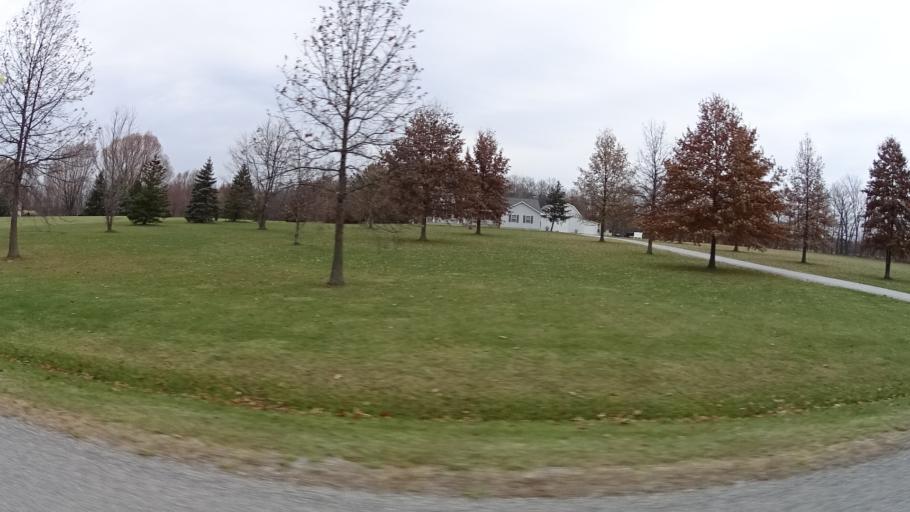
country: US
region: Ohio
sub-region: Lorain County
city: Lagrange
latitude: 41.1877
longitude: -82.0740
